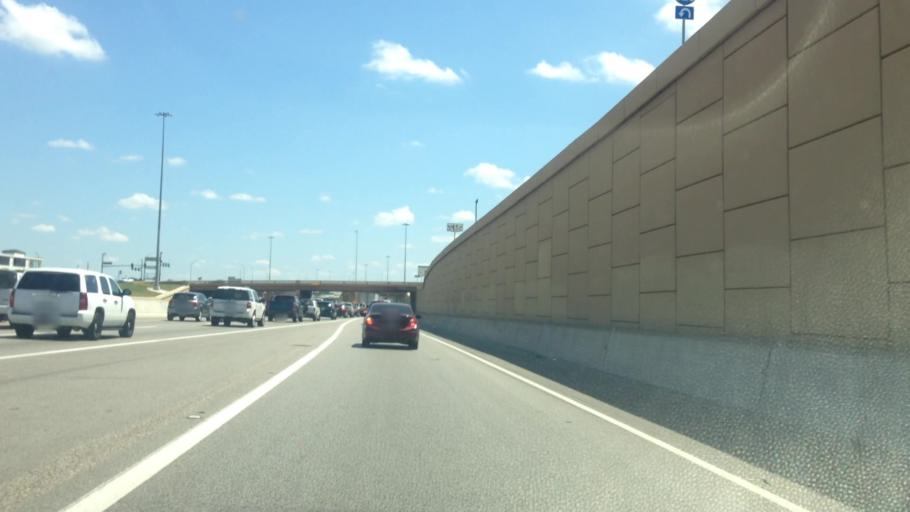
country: US
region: Texas
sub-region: Tarrant County
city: Watauga
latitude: 32.8391
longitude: -97.2674
